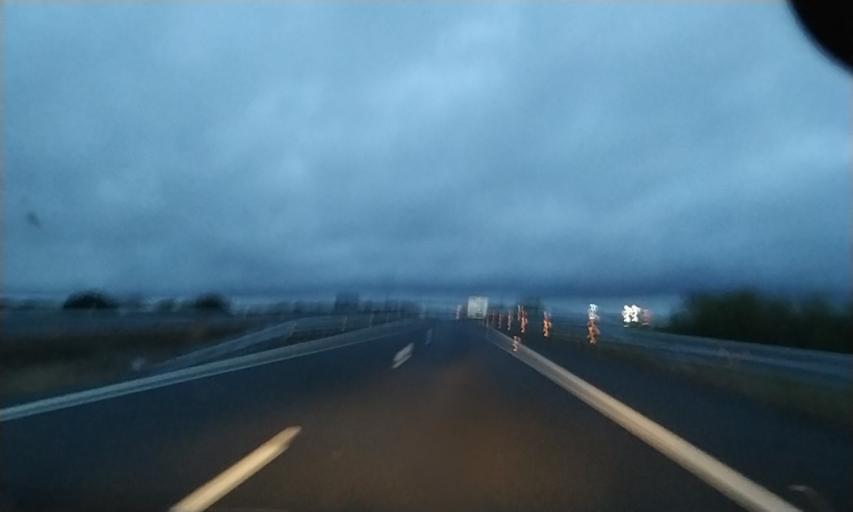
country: ES
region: Extremadura
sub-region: Provincia de Caceres
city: Aldea del Cano
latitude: 39.2796
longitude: -6.3255
